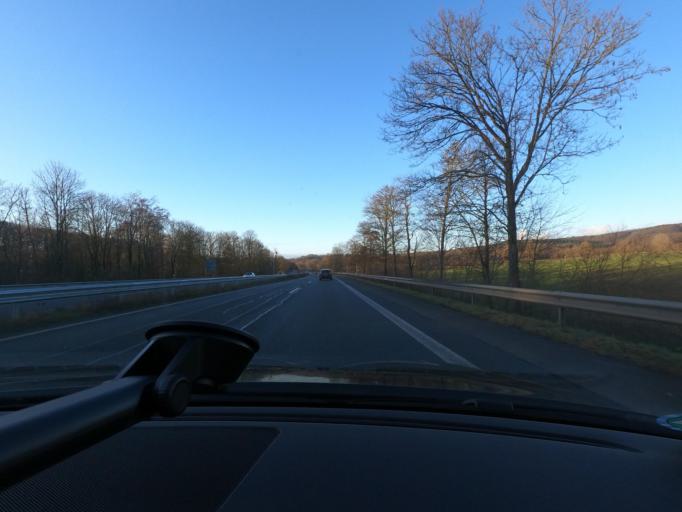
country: DE
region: Lower Saxony
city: Herzberg am Harz
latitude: 51.6669
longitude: 10.3217
